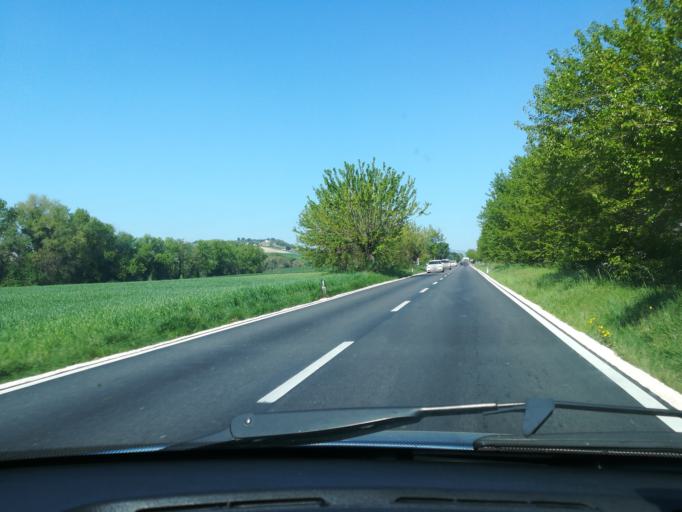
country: IT
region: The Marches
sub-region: Provincia di Macerata
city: Villa Potenza
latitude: 43.3248
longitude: 13.4105
